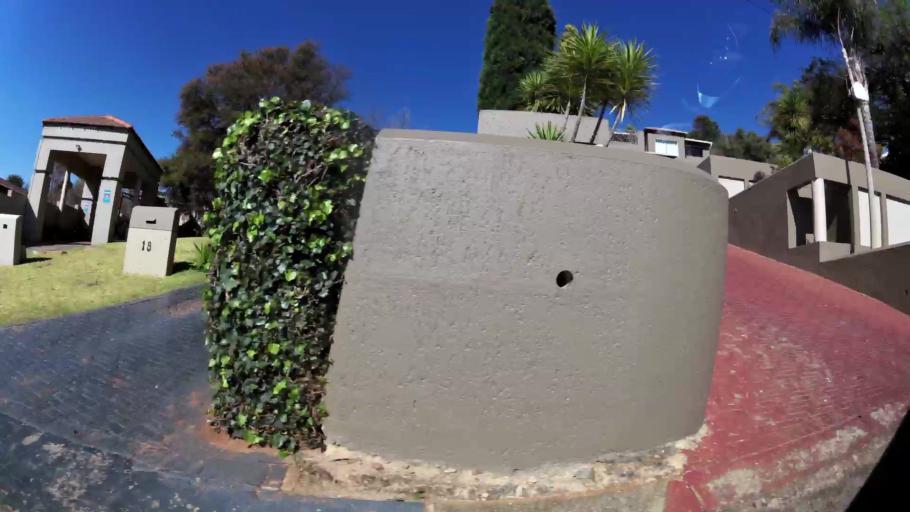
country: ZA
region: Gauteng
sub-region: City of Johannesburg Metropolitan Municipality
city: Roodepoort
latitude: -26.1213
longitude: 27.8701
